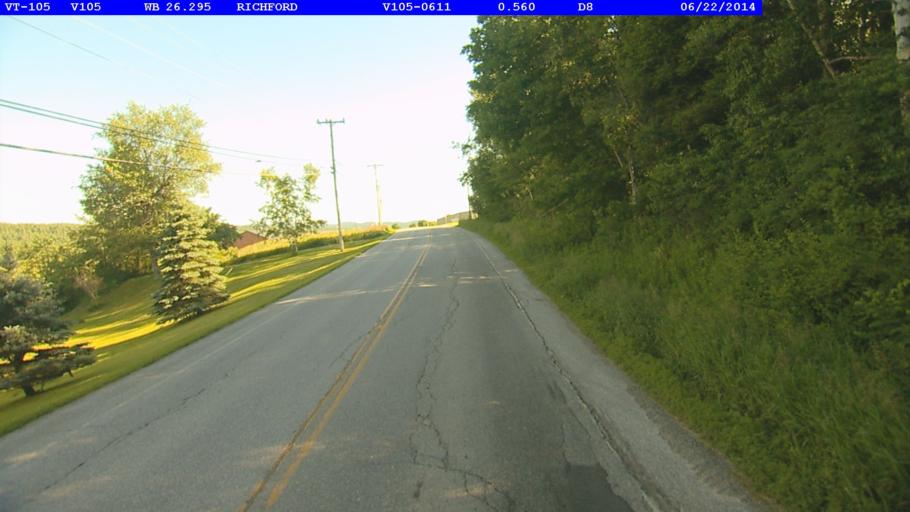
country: US
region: Vermont
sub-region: Franklin County
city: Richford
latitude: 44.9787
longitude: -72.6872
